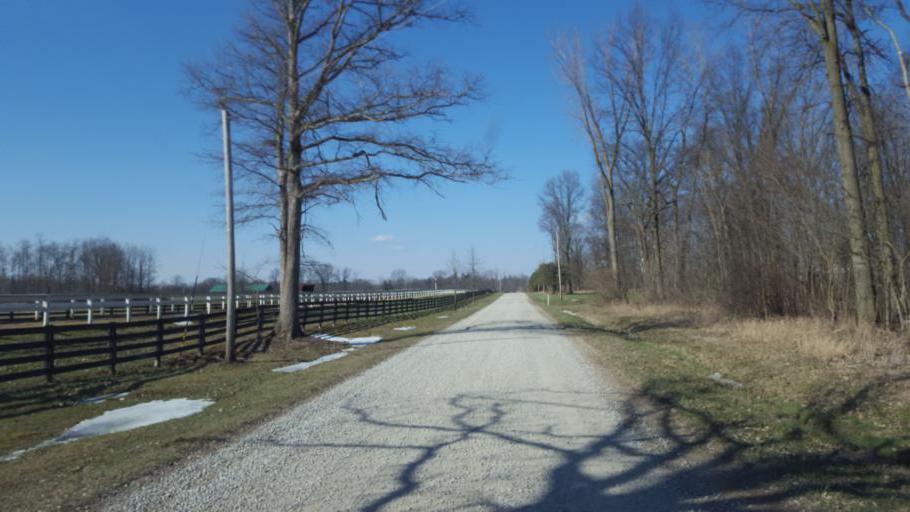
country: US
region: Ohio
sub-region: Morrow County
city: Mount Gilead
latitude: 40.5295
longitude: -82.7780
